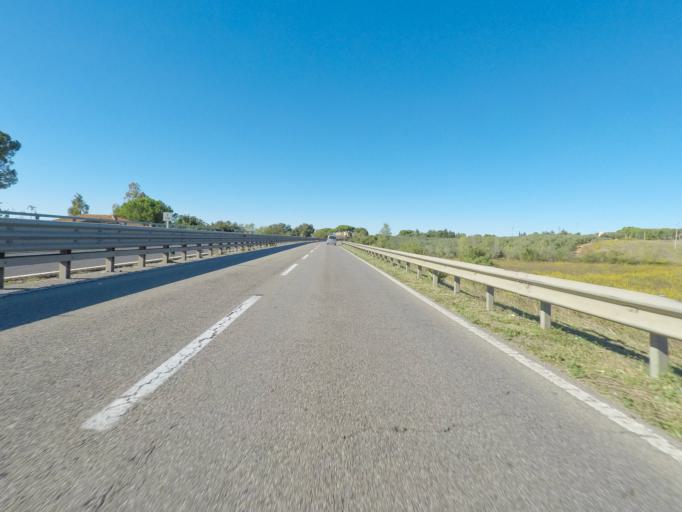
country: IT
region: Tuscany
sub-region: Provincia di Grosseto
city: Grosseto
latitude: 42.7209
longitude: 11.1394
